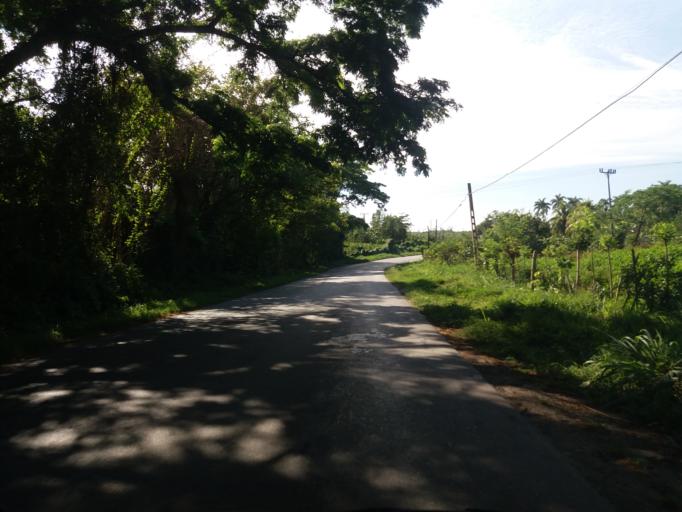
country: CU
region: Cienfuegos
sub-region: Municipio de Cienfuegos
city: Cienfuegos
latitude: 22.1618
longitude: -80.3651
